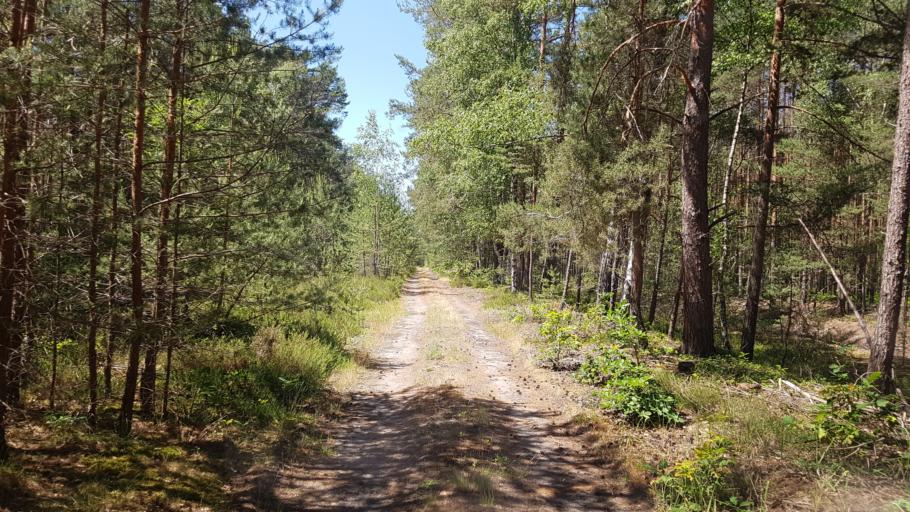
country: DE
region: Brandenburg
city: Ruckersdorf
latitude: 51.5461
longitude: 13.5509
